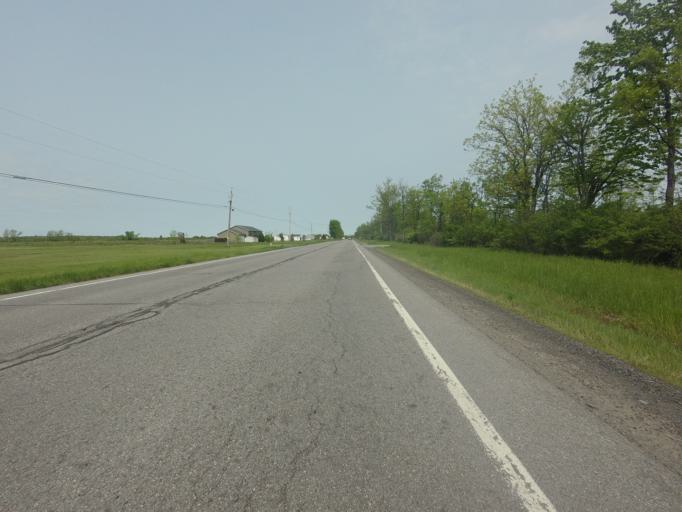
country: US
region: New York
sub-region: Jefferson County
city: Dexter
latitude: 44.0225
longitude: -76.0350
